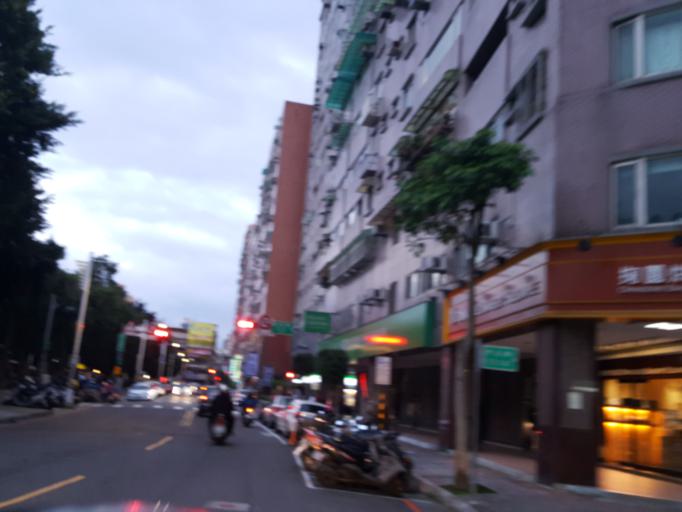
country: TW
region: Taipei
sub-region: Taipei
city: Banqiao
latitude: 24.9997
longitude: 121.5109
